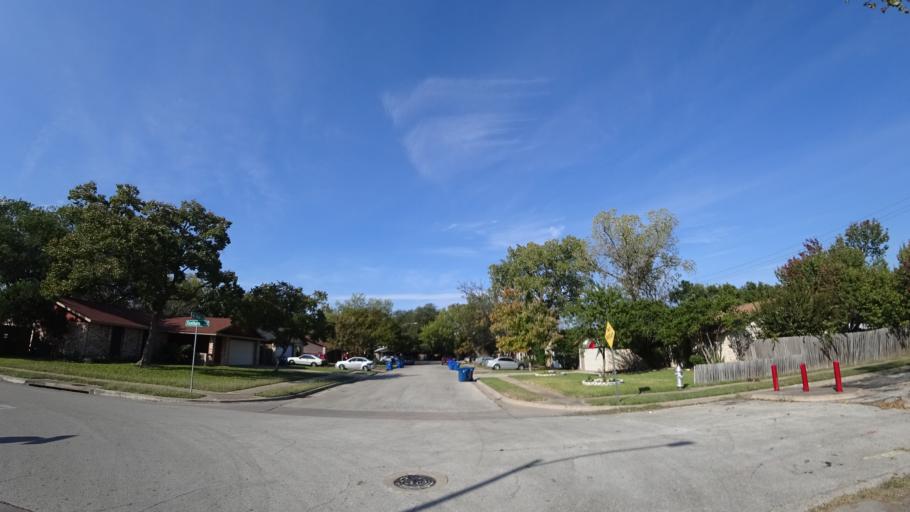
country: US
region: Texas
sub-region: Williamson County
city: Anderson Mill
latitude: 30.4560
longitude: -97.7997
